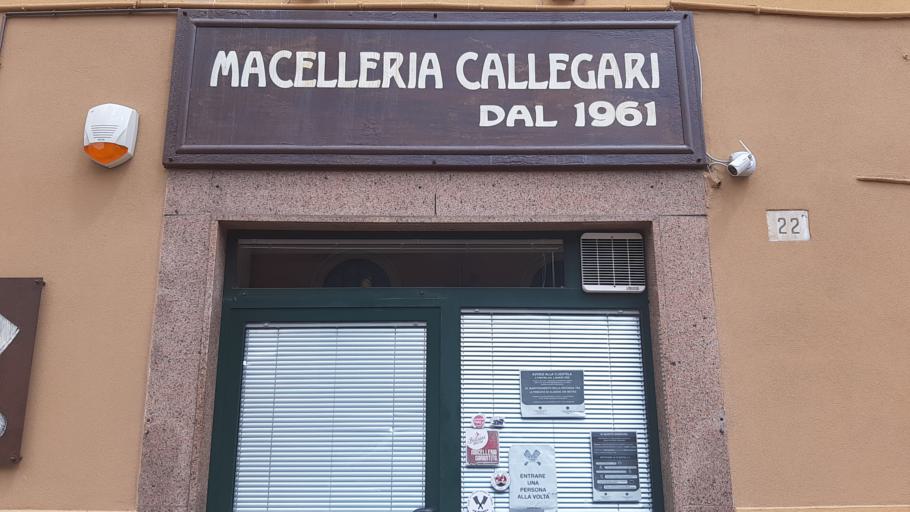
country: IT
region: Emilia-Romagna
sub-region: Provincia di Piacenza
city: Piacenza
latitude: 45.0474
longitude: 9.6947
